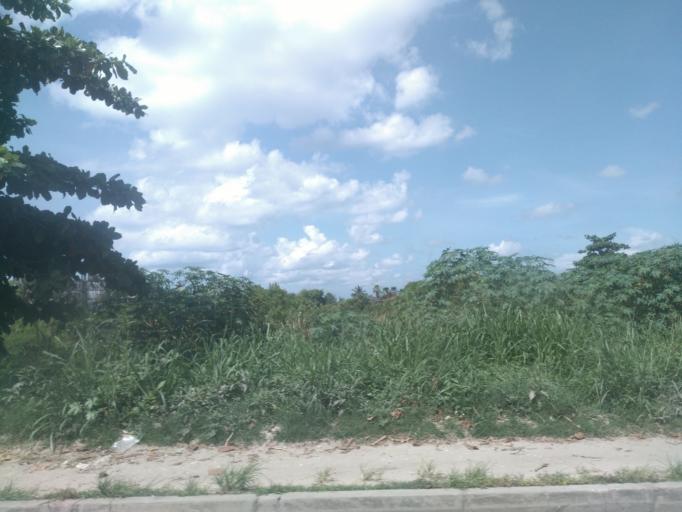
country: TZ
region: Zanzibar Urban/West
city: Zanzibar
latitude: -6.1591
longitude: 39.1998
